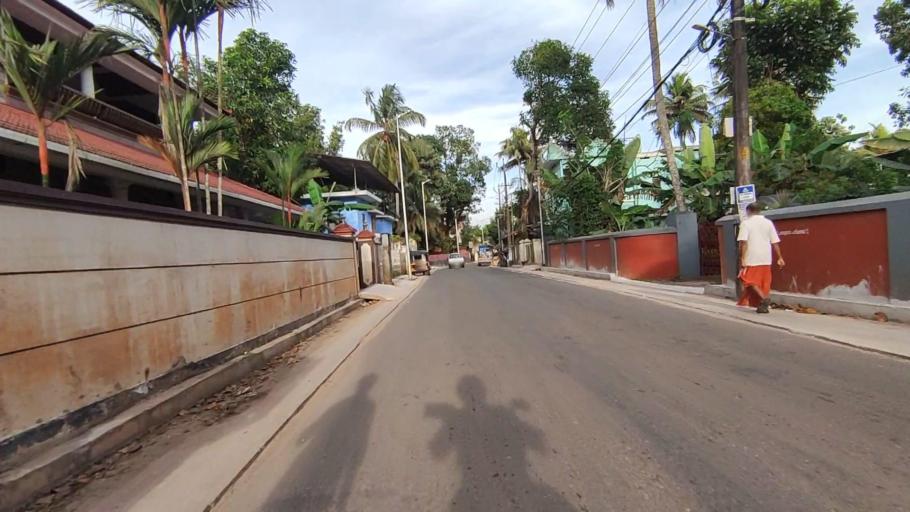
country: IN
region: Kerala
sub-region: Kottayam
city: Kottayam
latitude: 9.6129
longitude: 76.5057
